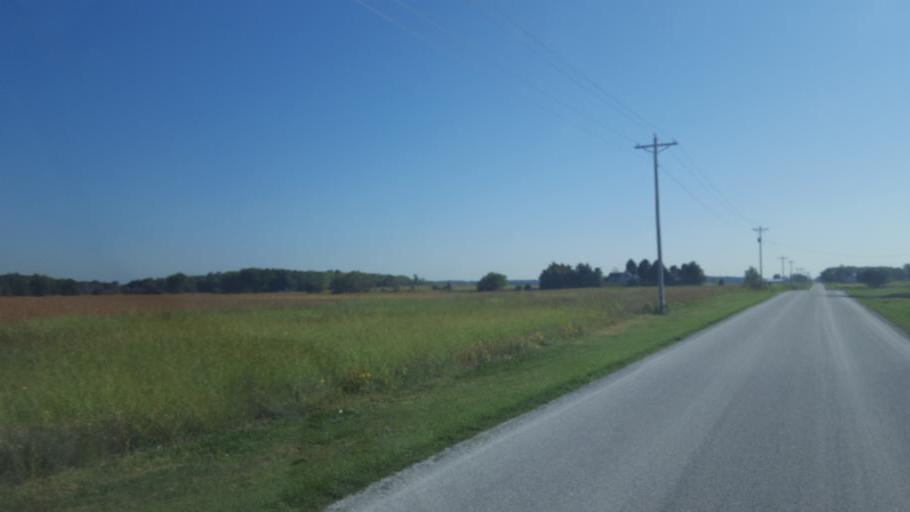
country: US
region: Ohio
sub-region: Hardin County
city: Kenton
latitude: 40.5809
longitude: -83.5458
